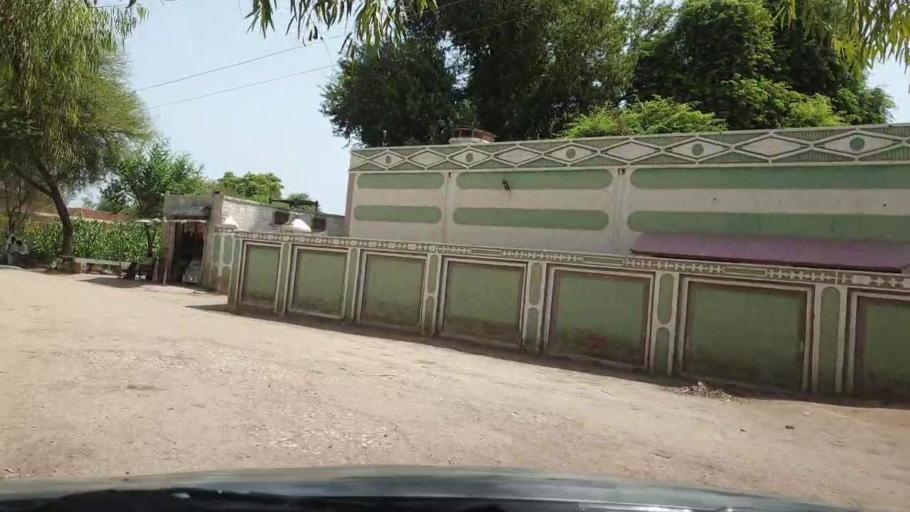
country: PK
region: Sindh
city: Pano Aqil
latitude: 27.9081
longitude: 69.1517
